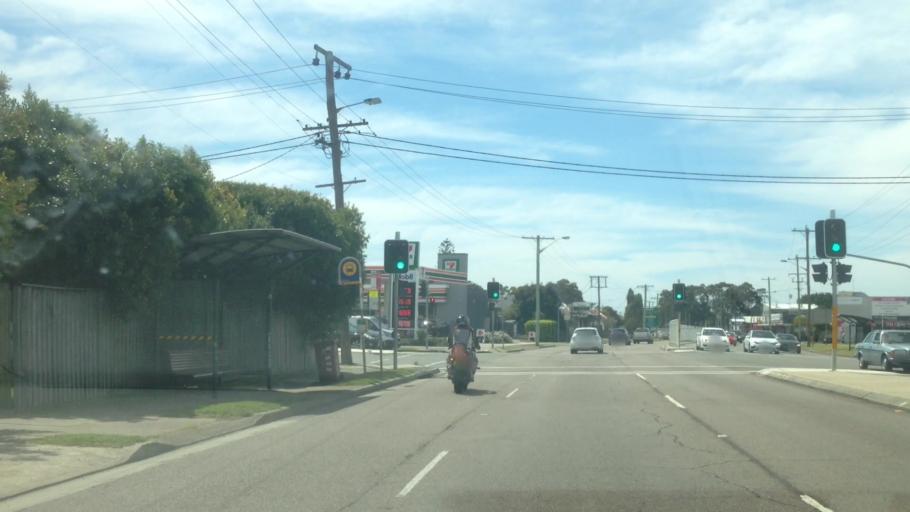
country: AU
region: New South Wales
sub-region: Newcastle
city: Broadmeadow
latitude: -32.9185
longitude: 151.7243
